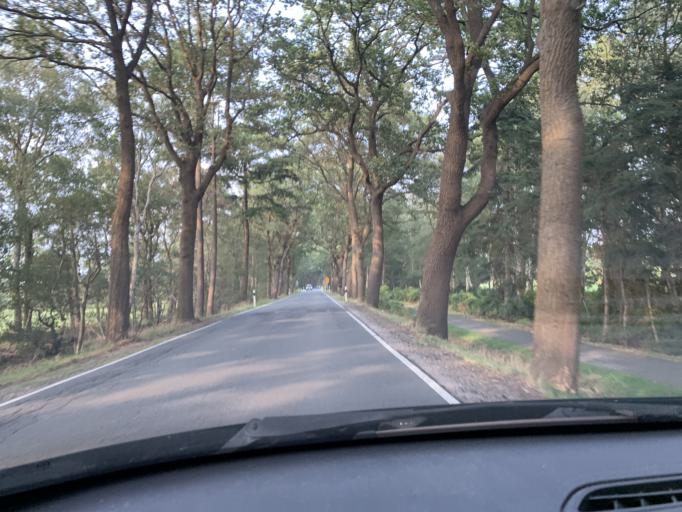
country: DE
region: Lower Saxony
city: Apen
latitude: 53.1924
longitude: 7.7856
